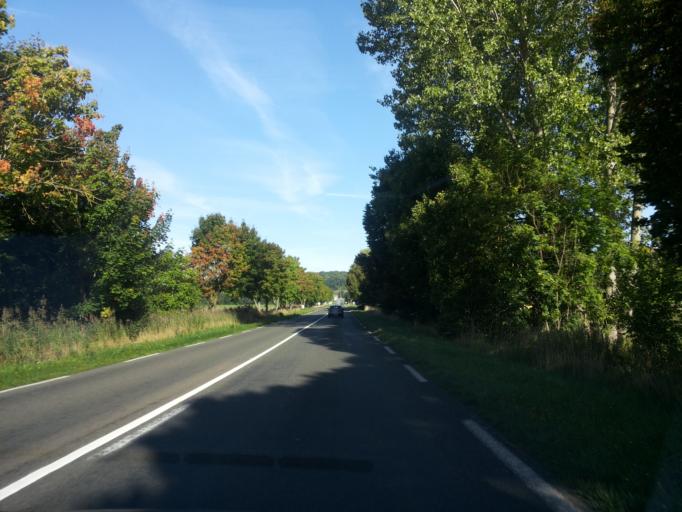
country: FR
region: Picardie
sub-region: Departement de l'Aisne
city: Crepy
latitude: 49.6019
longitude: 3.5114
